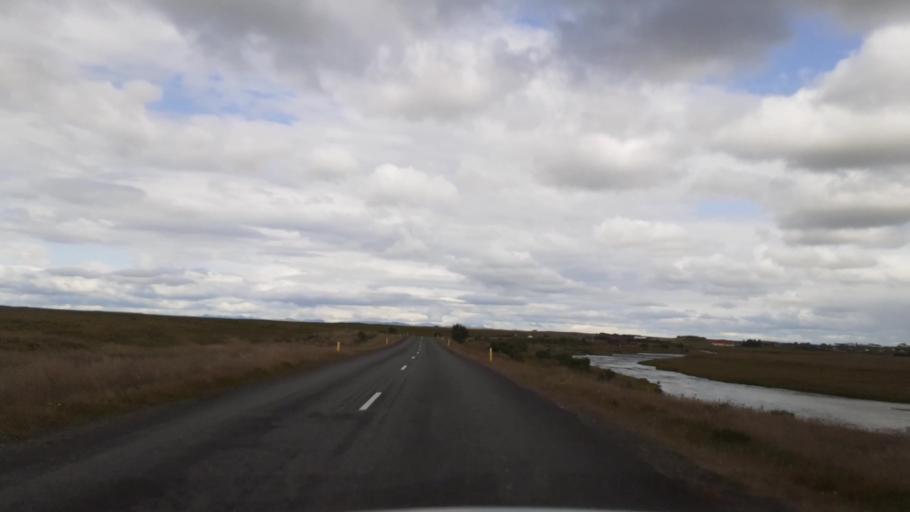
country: IS
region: South
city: Vestmannaeyjar
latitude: 63.8230
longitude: -20.4273
